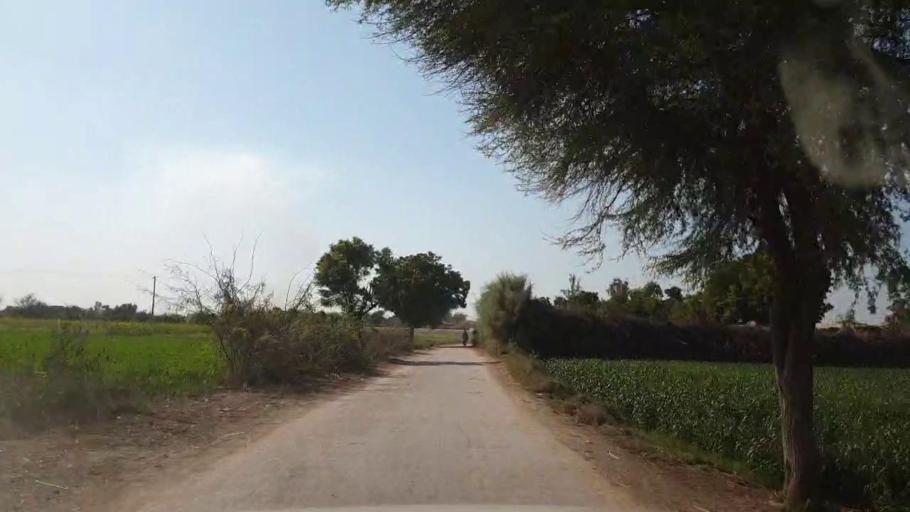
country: PK
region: Sindh
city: Tando Allahyar
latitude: 25.4825
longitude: 68.6802
